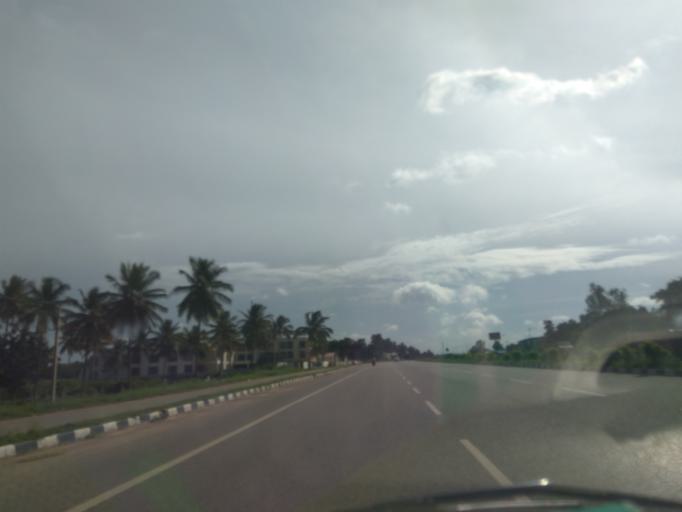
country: IN
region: Karnataka
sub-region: Bangalore Rural
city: Hoskote
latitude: 13.0808
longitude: 77.8146
